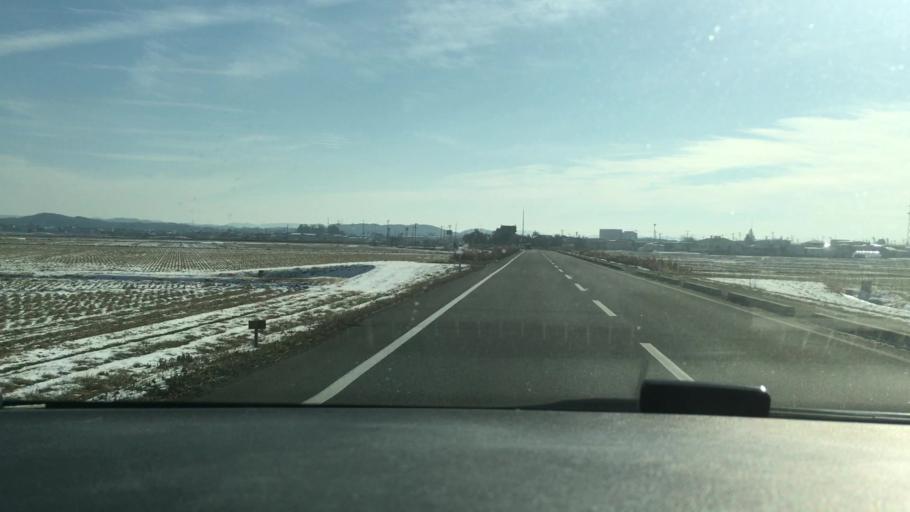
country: JP
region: Iwate
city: Ichinoseki
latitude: 38.7795
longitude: 141.1272
